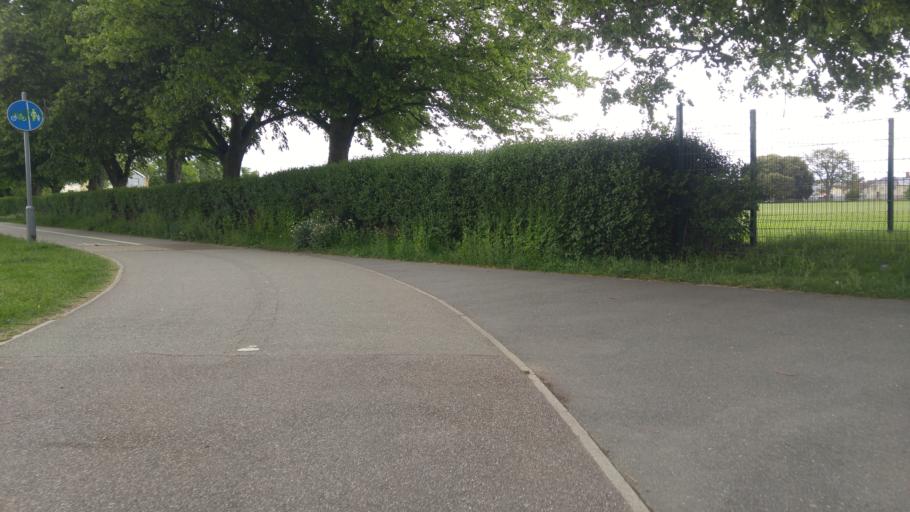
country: GB
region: England
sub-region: Essex
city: Colchester
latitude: 51.8811
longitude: 0.9012
